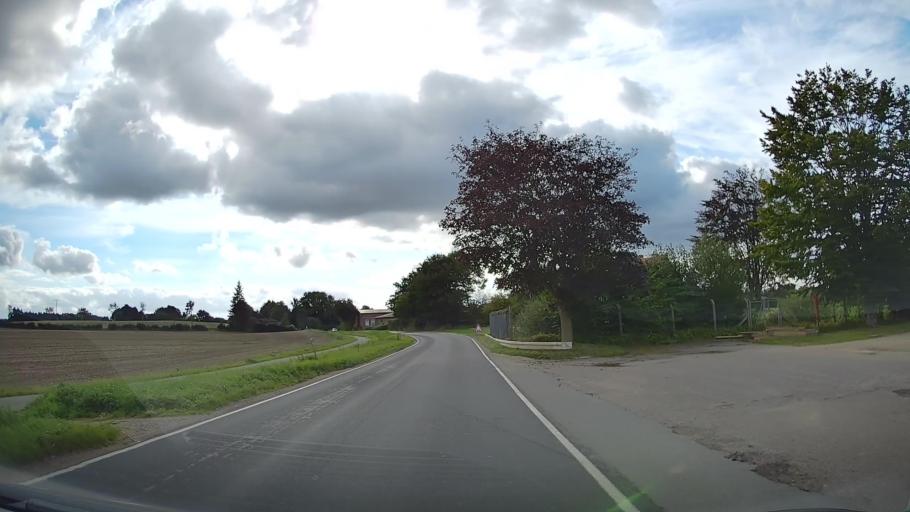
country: DE
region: Schleswig-Holstein
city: Niesgrau
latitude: 54.7665
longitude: 9.8062
